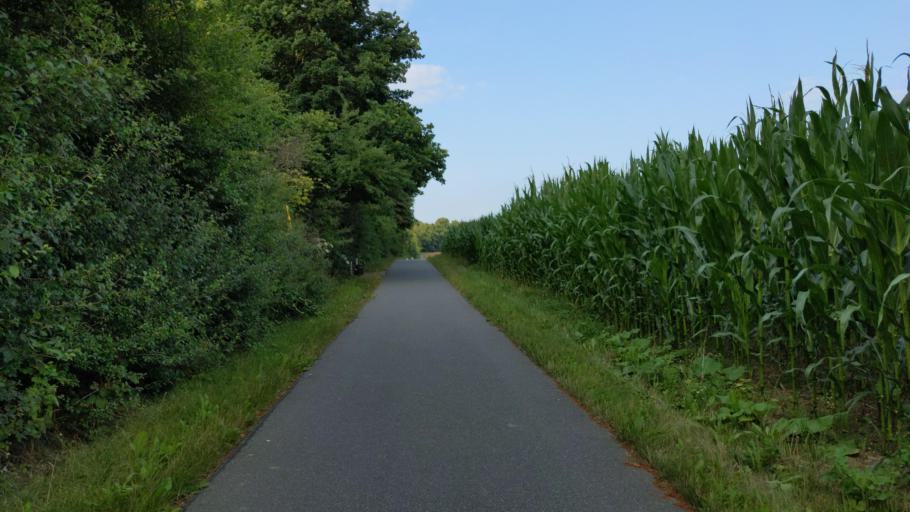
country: DE
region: Mecklenburg-Vorpommern
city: Dassow
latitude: 53.8983
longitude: 10.9346
